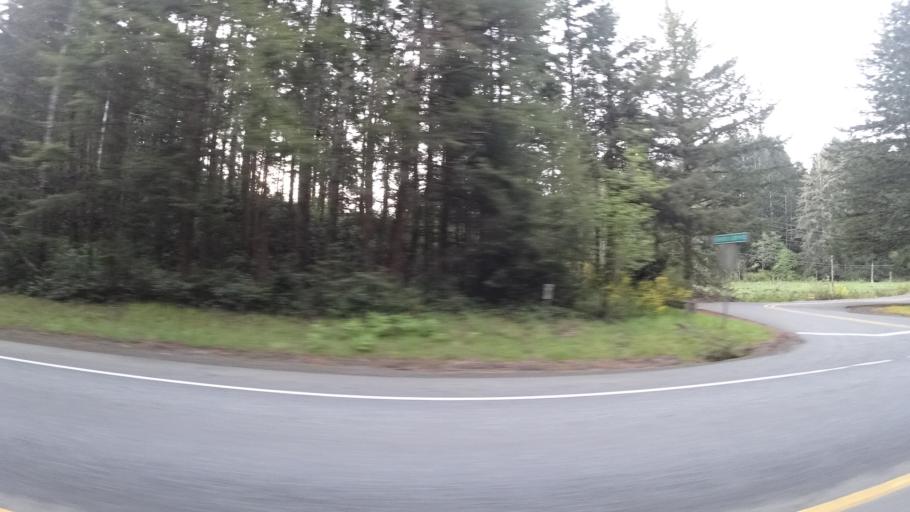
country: US
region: Oregon
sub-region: Coos County
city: Lakeside
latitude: 43.5557
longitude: -124.2082
